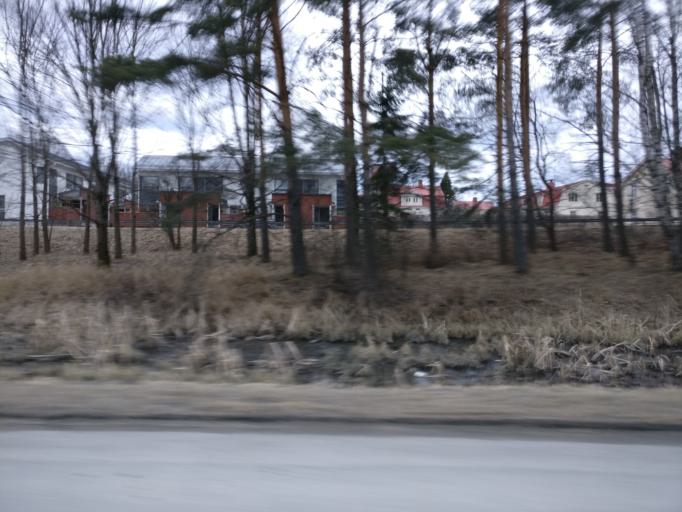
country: FI
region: Haeme
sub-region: Haemeenlinna
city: Haemeenlinna
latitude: 60.9964
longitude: 24.4540
